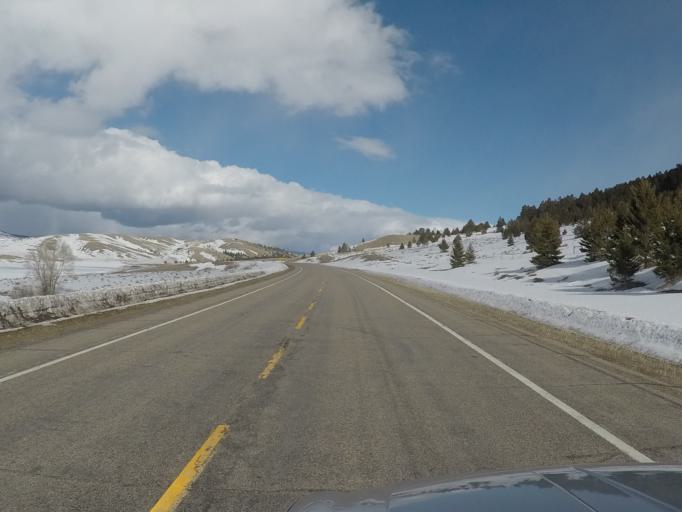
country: US
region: Montana
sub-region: Meagher County
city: White Sulphur Springs
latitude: 46.6182
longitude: -110.7424
